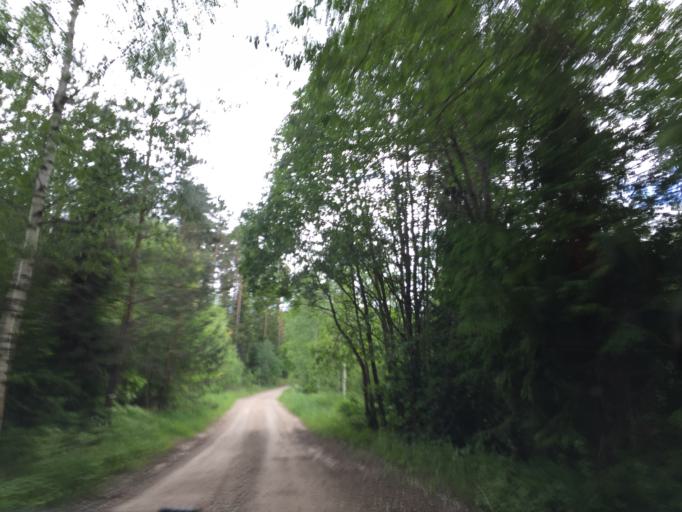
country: LV
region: Apes Novads
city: Ape
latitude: 57.5428
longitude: 26.4098
